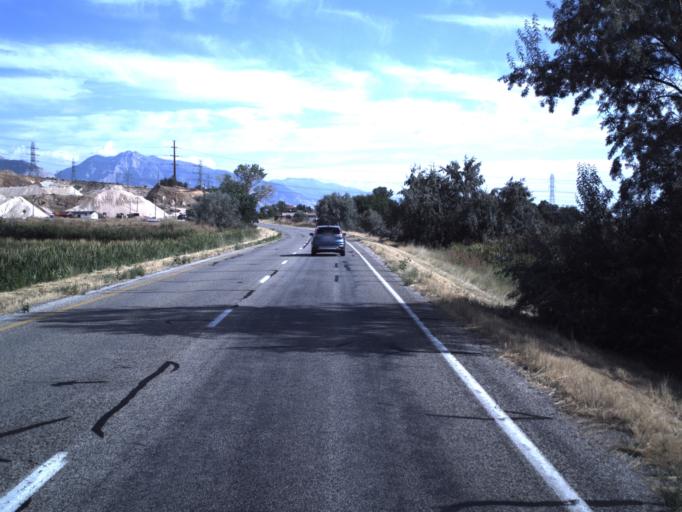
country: US
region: Utah
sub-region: Box Elder County
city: South Willard
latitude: 41.3435
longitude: -112.0339
